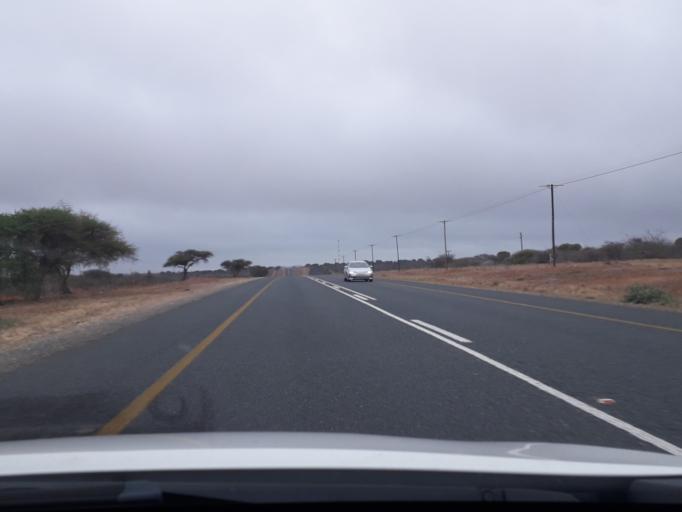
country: ZA
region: Limpopo
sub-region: Vhembe District Municipality
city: Louis Trichardt
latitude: -23.4166
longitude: 29.7532
